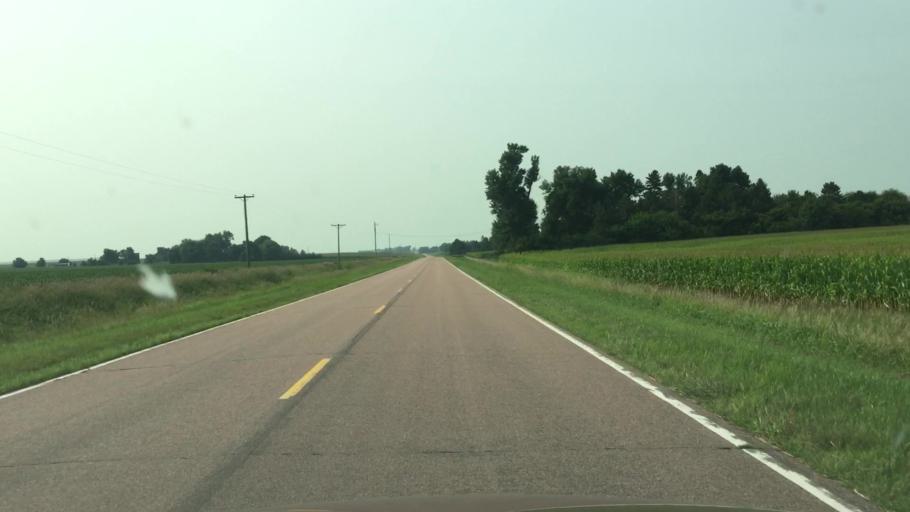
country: US
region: Iowa
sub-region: O'Brien County
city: Sheldon
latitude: 43.2506
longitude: -95.7832
